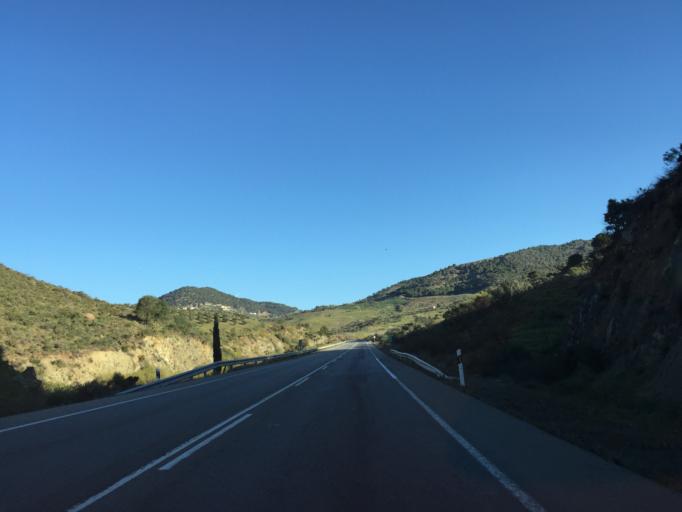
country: ES
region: Andalusia
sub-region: Provincia de Malaga
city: Carratraca
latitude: 36.8345
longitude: -4.8077
